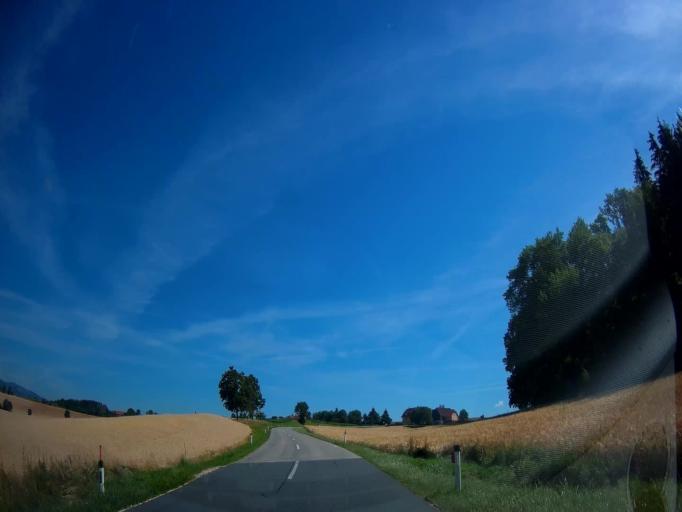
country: AT
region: Carinthia
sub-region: Politischer Bezirk Sankt Veit an der Glan
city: Sankt Veit an der Glan
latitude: 46.7388
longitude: 14.3995
